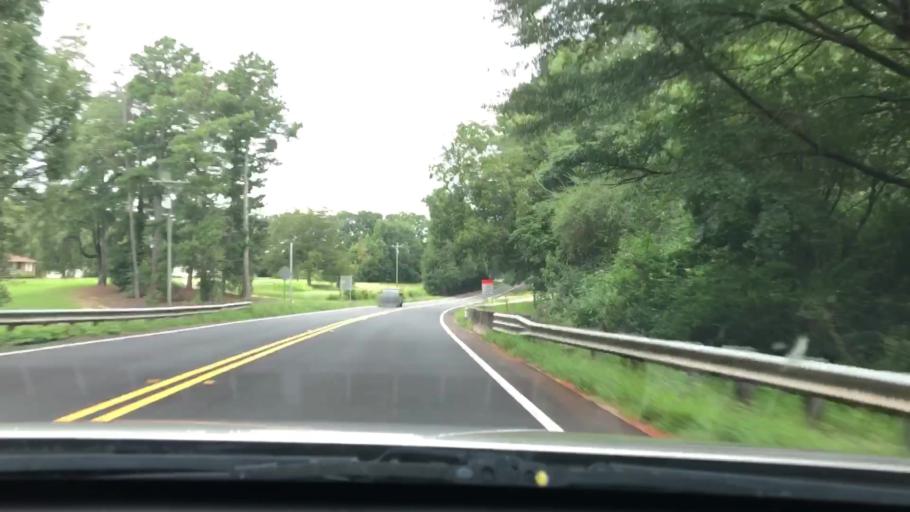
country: US
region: Georgia
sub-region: Pike County
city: Zebulon
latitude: 33.0363
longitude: -84.3744
